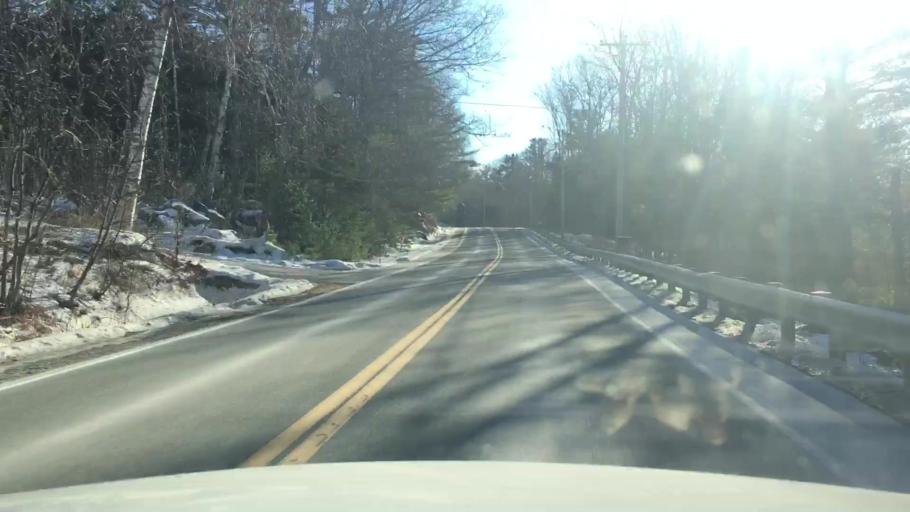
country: US
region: Maine
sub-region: Hancock County
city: Orland
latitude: 44.5401
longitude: -68.7457
